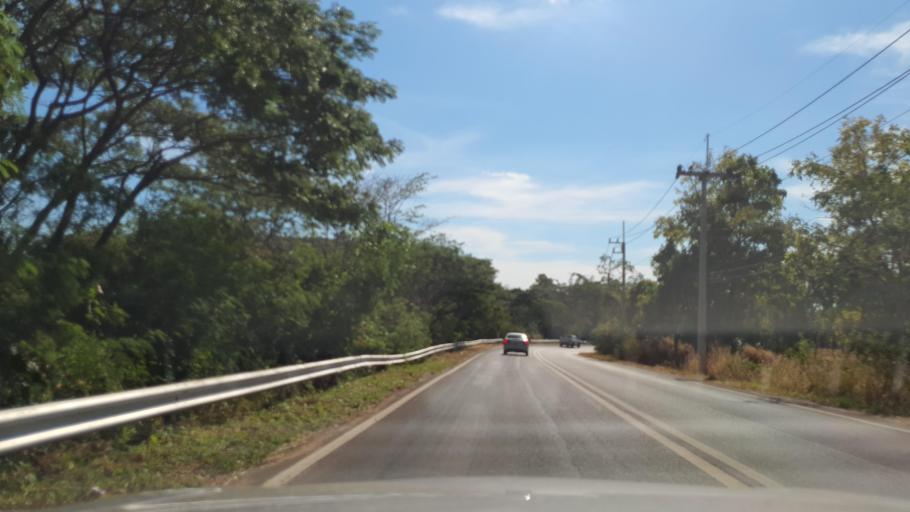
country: TH
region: Kalasin
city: Khao Wong
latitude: 16.7520
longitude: 104.1191
